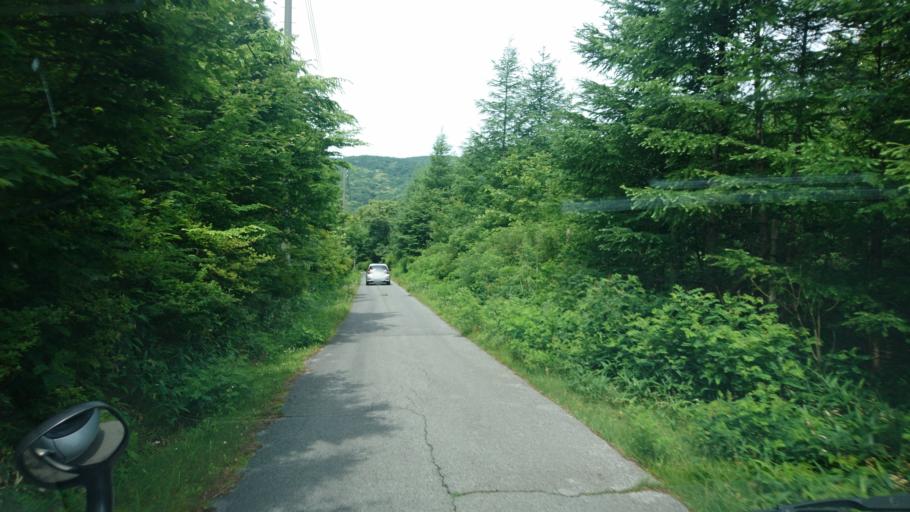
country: JP
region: Iwate
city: Ofunato
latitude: 39.1638
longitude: 141.7531
